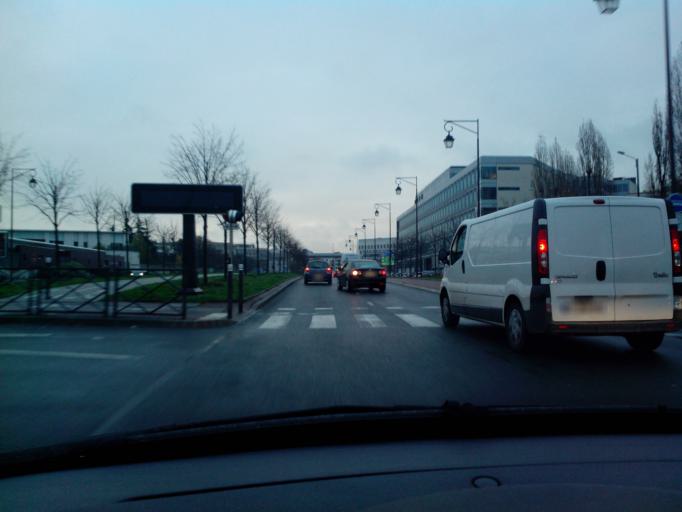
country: FR
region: Ile-de-France
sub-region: Departement des Hauts-de-Seine
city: Antony
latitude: 48.7631
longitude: 2.3055
